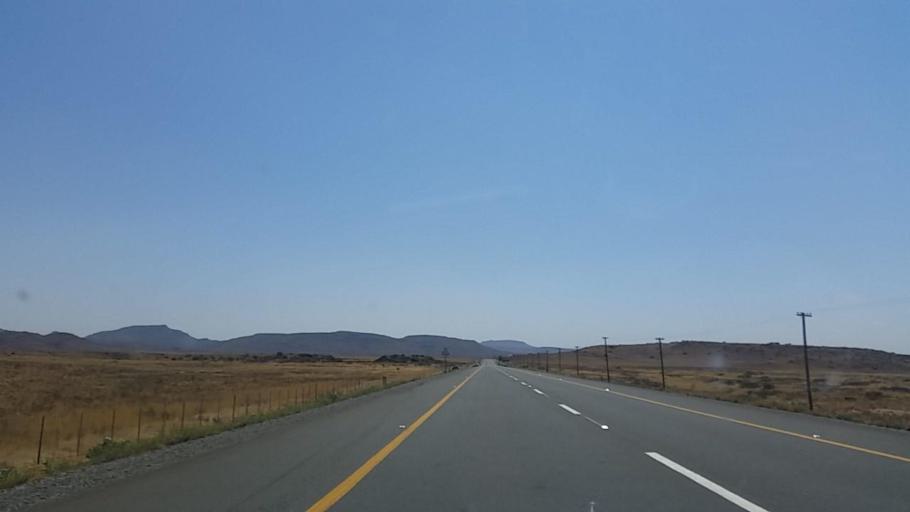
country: ZA
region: Eastern Cape
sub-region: Chris Hani District Municipality
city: Middelburg
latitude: -31.4447
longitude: 25.0209
